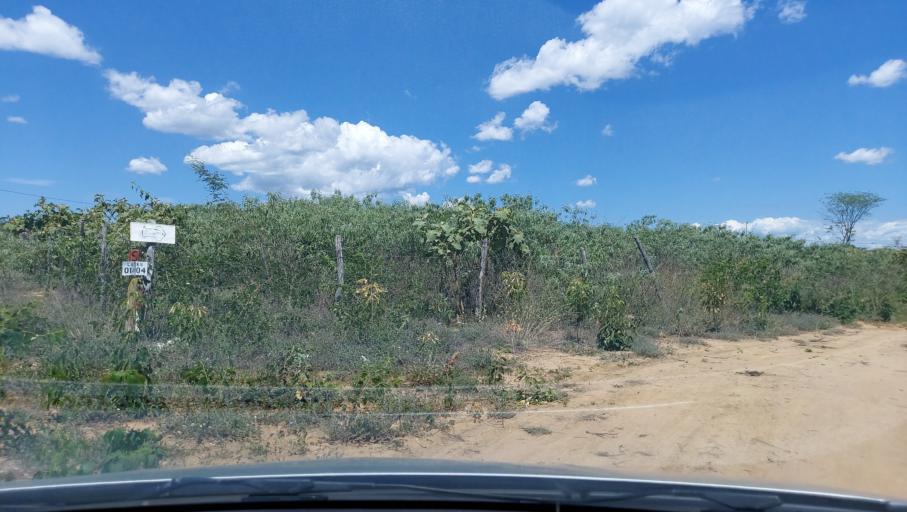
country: BR
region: Bahia
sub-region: Oliveira Dos Brejinhos
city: Beira Rio
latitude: -12.0077
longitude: -42.6357
